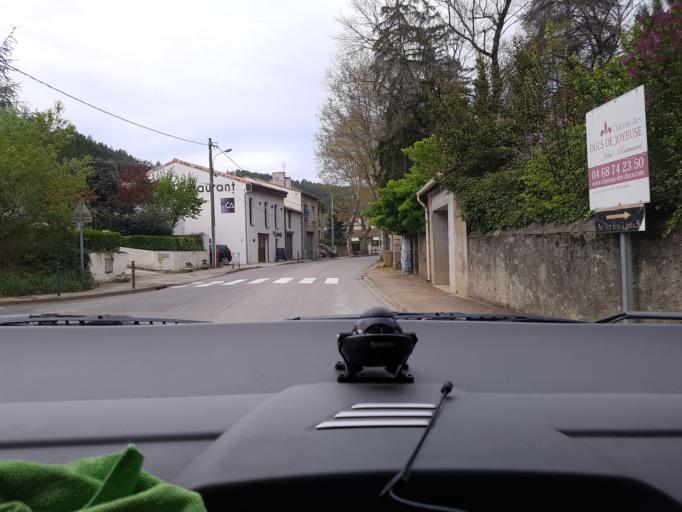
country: FR
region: Languedoc-Roussillon
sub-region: Departement de l'Aude
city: Couiza
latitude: 42.9407
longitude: 2.2525
